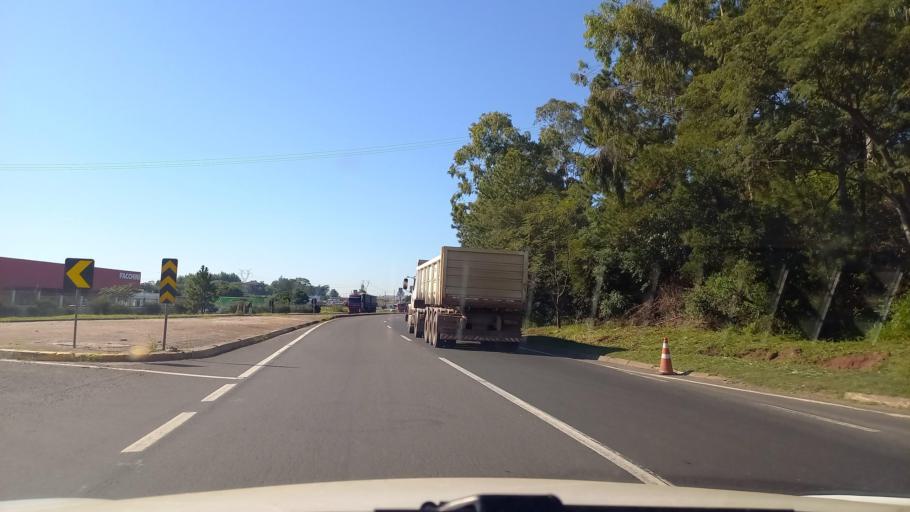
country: BR
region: Rio Grande do Sul
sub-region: Esteio
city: Esteio
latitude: -29.8458
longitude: -51.2782
